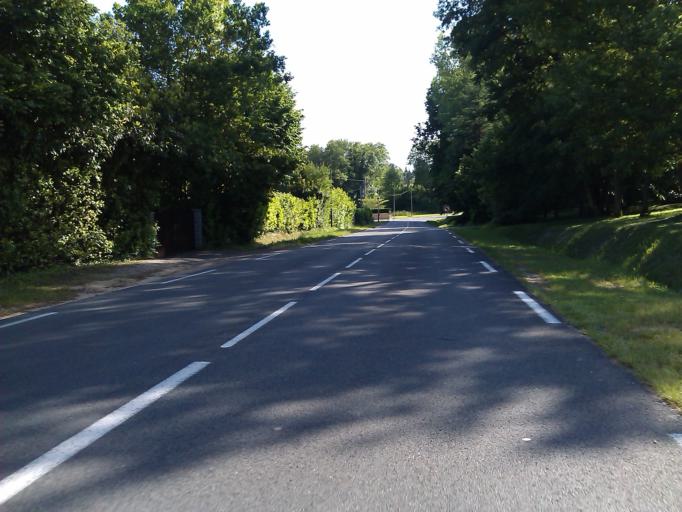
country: FR
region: Aquitaine
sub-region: Departement de la Gironde
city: Peujard
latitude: 45.0442
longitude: -0.4301
